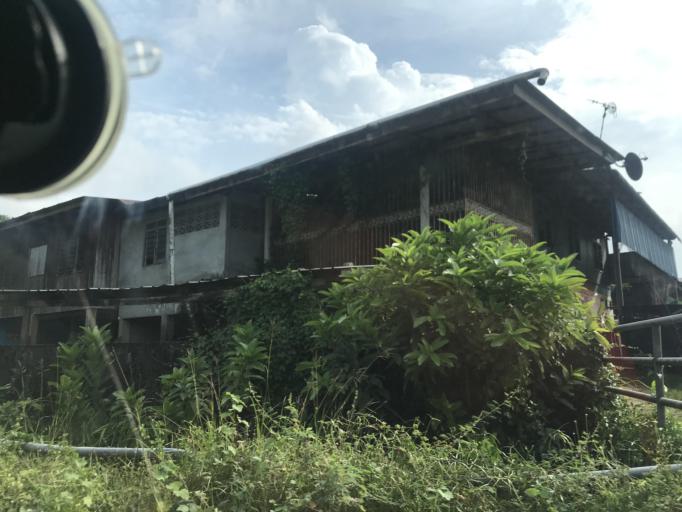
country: MY
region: Kelantan
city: Kota Bharu
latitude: 6.1133
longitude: 102.2366
